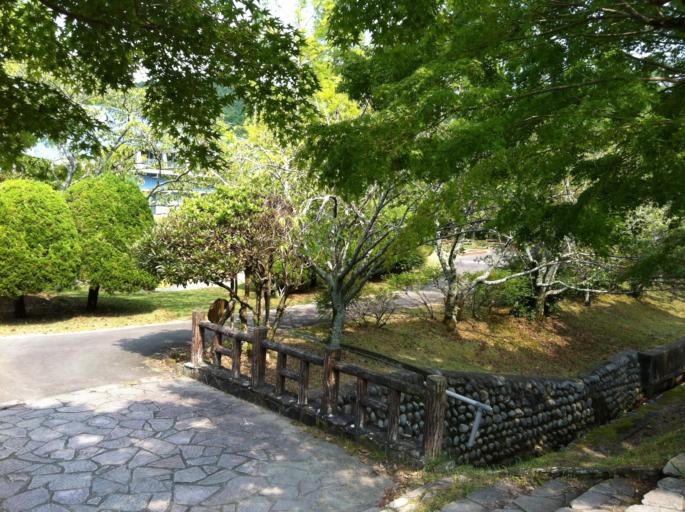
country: JP
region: Shizuoka
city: Shimada
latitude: 34.8498
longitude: 138.1744
